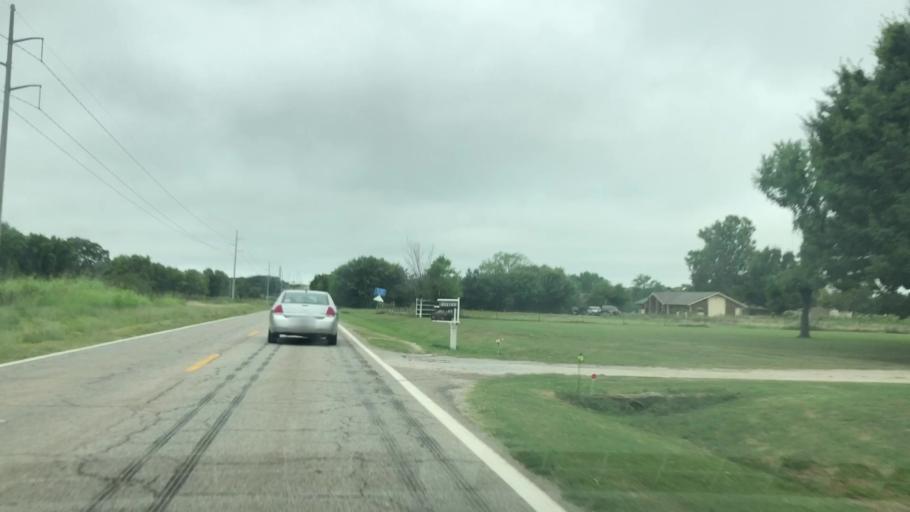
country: US
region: Oklahoma
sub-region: Washington County
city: Dewey
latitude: 36.7280
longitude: -95.8426
